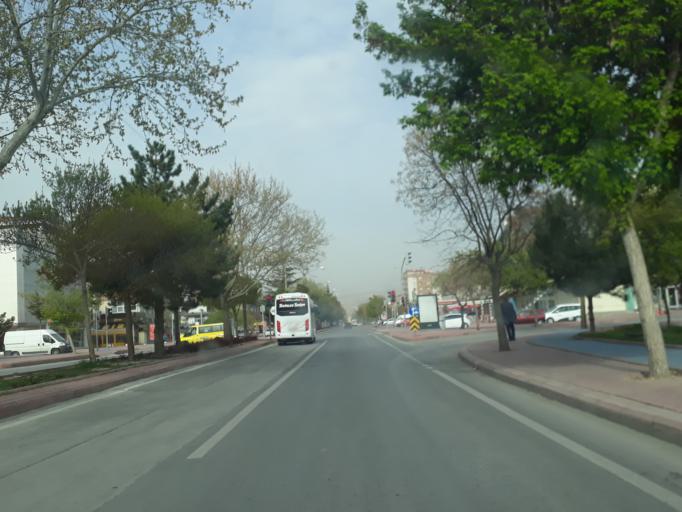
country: TR
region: Konya
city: Selcuklu
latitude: 37.9372
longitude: 32.5042
